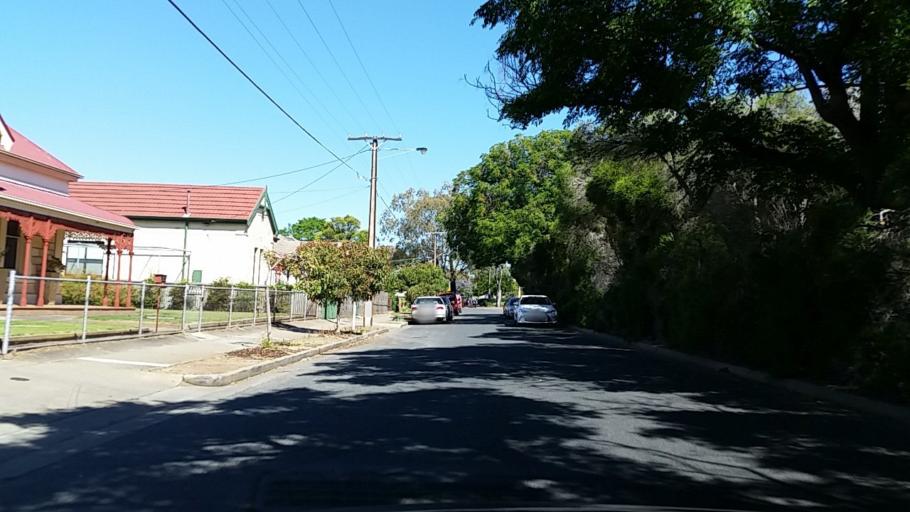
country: AU
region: South Australia
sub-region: Charles Sturt
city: Allenby Gardens
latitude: -34.8961
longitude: 138.5629
